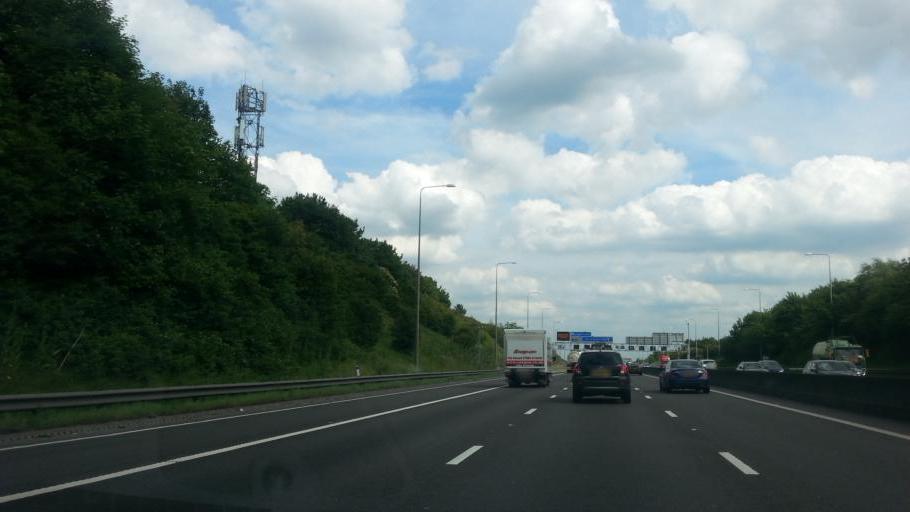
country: GB
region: England
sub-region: City and Borough of Leeds
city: Morley
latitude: 53.7338
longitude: -1.6137
